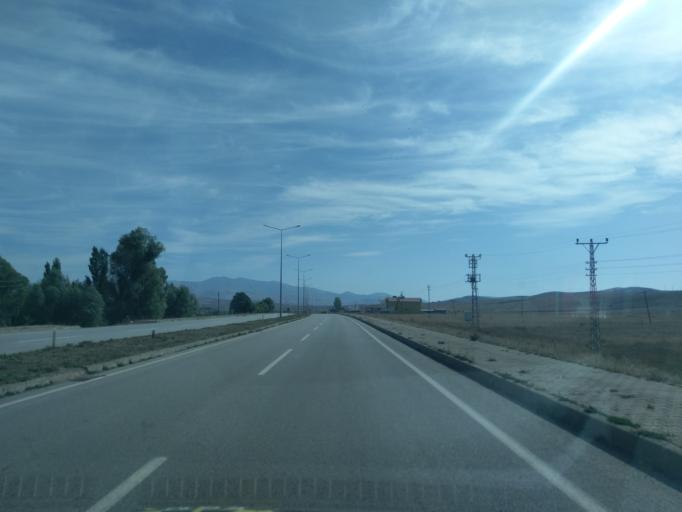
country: TR
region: Sivas
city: Imranli
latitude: 39.8708
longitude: 38.1296
